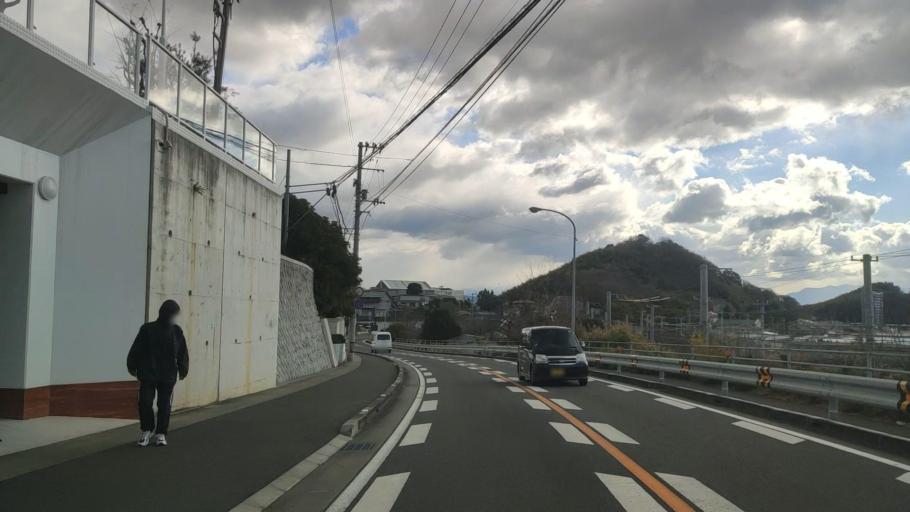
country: JP
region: Ehime
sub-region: Shikoku-chuo Shi
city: Matsuyama
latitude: 33.8769
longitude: 132.7054
